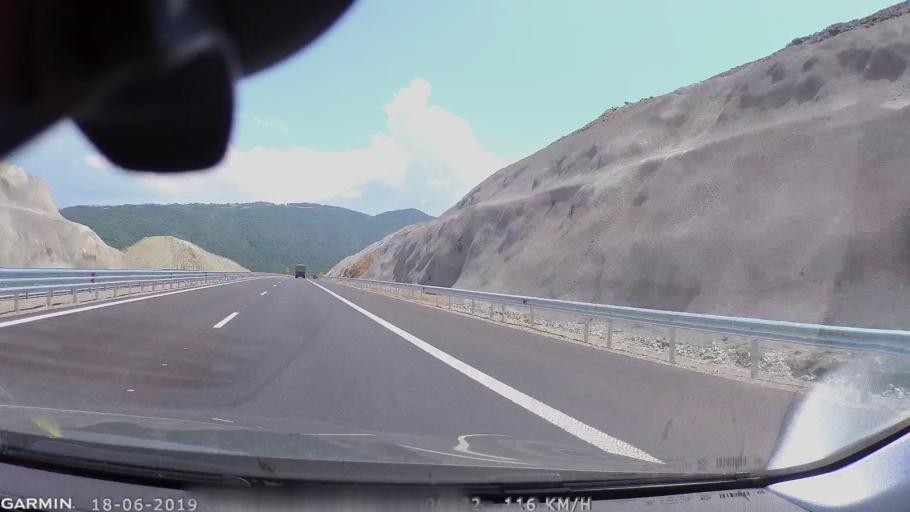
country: BG
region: Blagoevgrad
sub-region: Obshtina Blagoevgrad
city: Blagoevgrad
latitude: 41.9689
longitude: 23.0882
